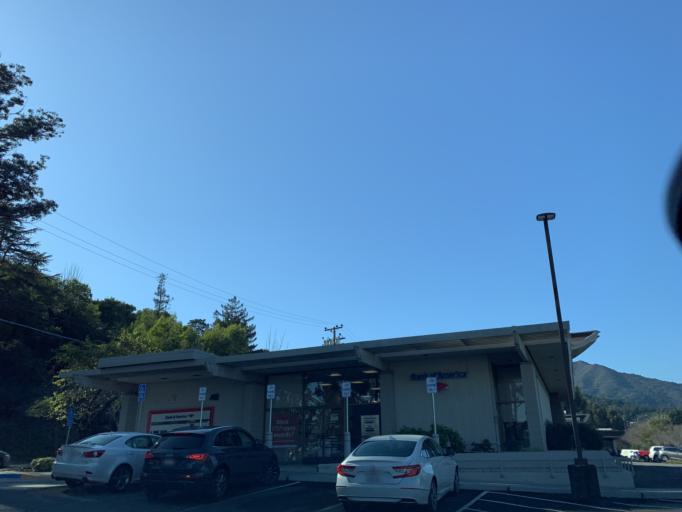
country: US
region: California
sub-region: Marin County
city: Corte Madera
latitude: 37.9250
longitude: -122.5188
